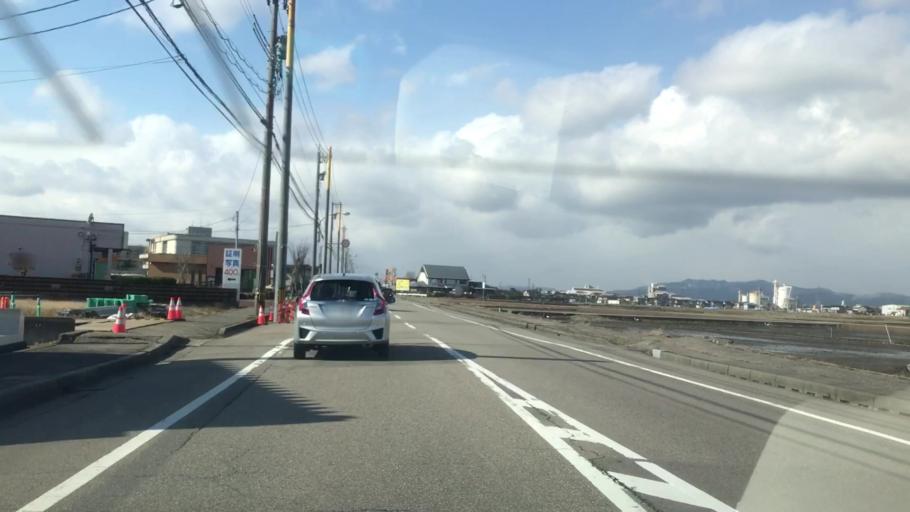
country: JP
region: Toyama
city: Nishishinminato
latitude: 36.7243
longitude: 137.0673
